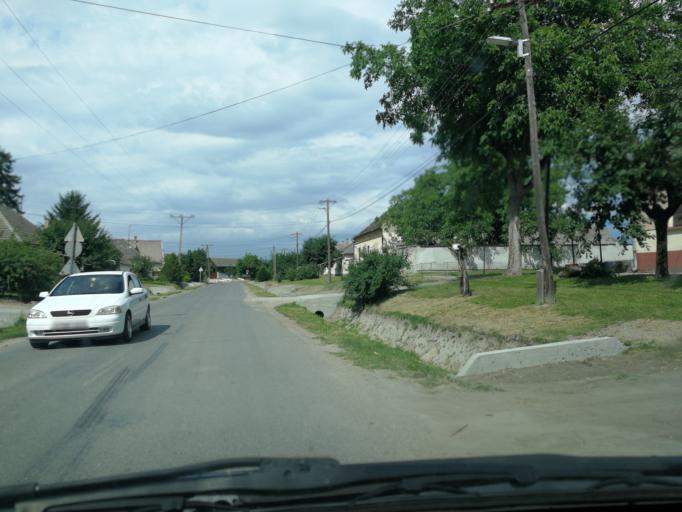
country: HU
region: Bacs-Kiskun
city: Dusnok
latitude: 46.4408
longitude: 19.0243
